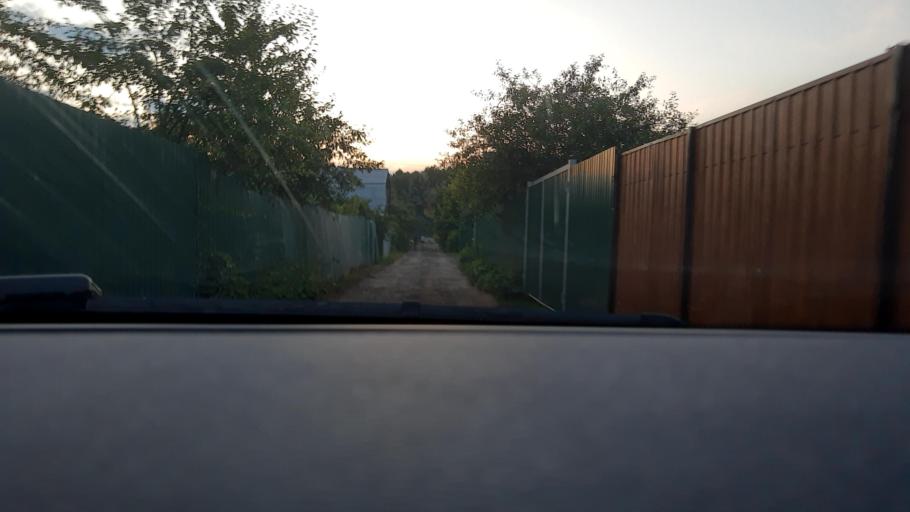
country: RU
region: Nizjnij Novgorod
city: Kstovo
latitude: 56.1553
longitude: 44.2569
